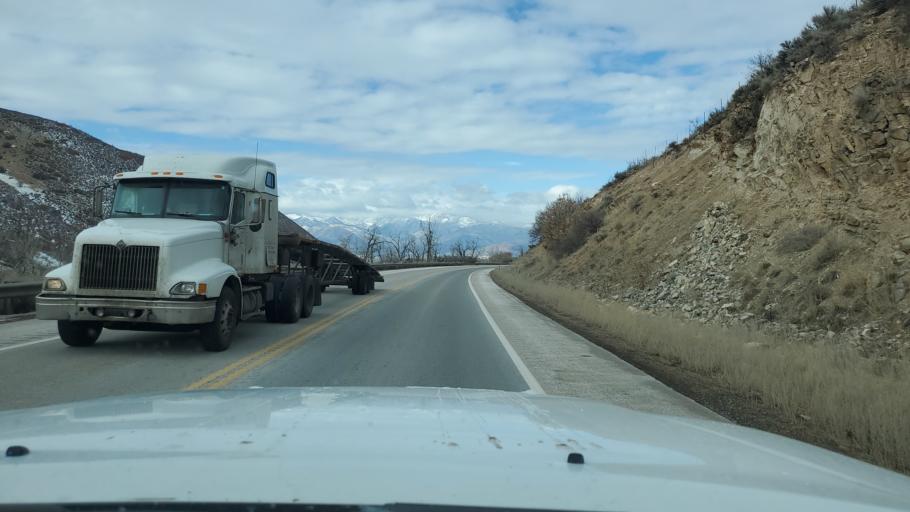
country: US
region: Utah
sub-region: Wasatch County
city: Heber
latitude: 40.4460
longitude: -111.3654
